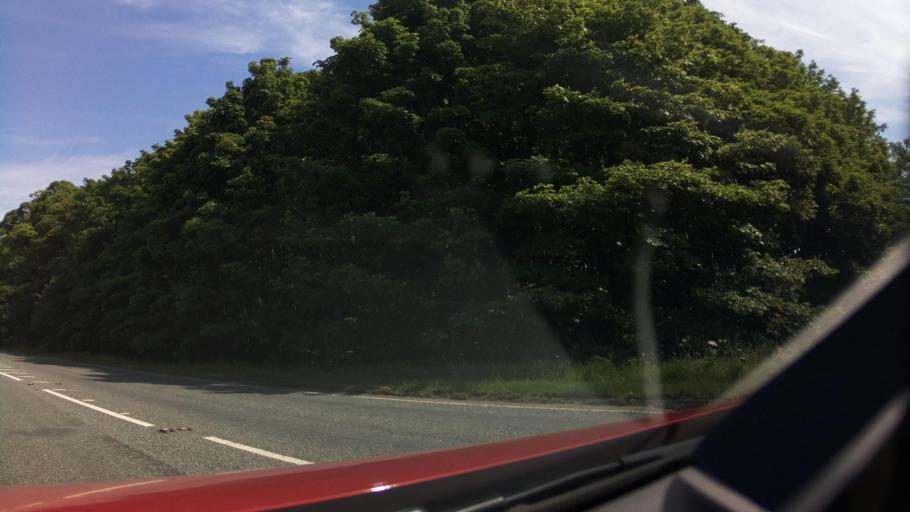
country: GB
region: England
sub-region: Lincolnshire
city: Burton
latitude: 53.3609
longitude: -0.5454
